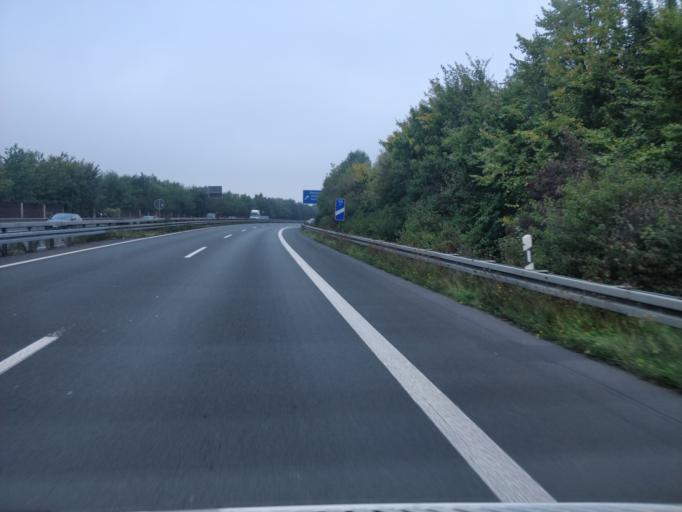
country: DE
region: North Rhine-Westphalia
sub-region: Regierungsbezirk Dusseldorf
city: Dinslaken
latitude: 51.5350
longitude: 6.7523
